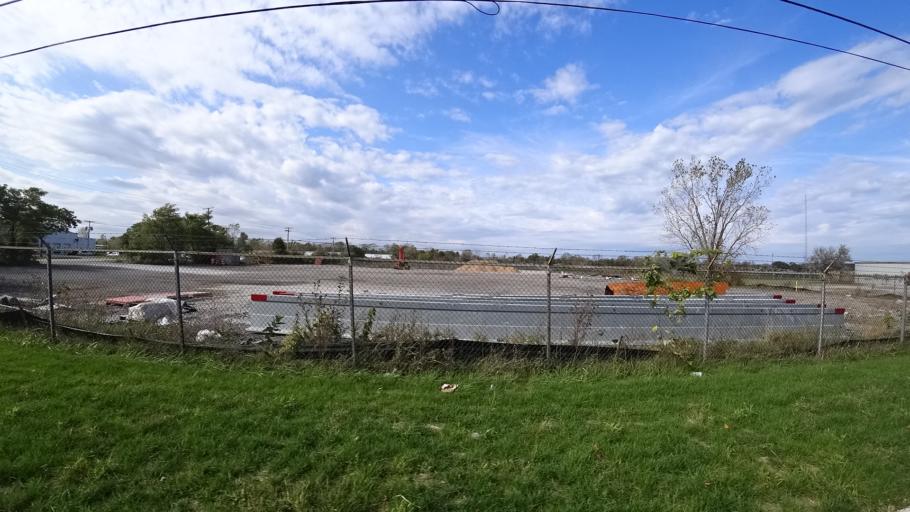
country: US
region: Indiana
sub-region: LaPorte County
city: Michigan City
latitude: 41.6730
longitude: -86.9037
